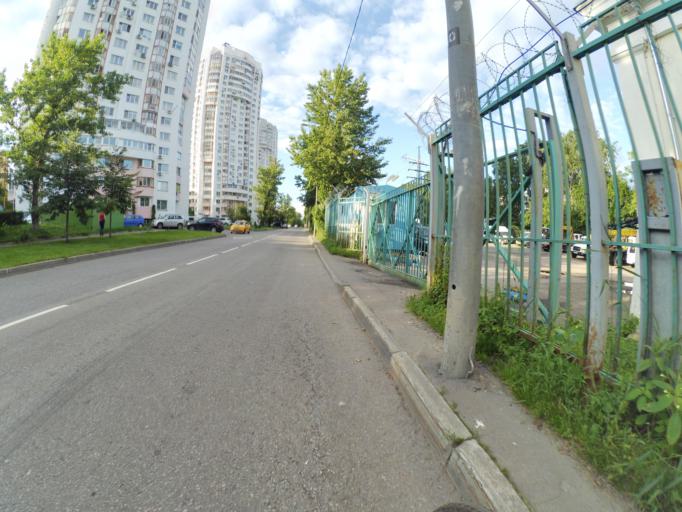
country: RU
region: Moscow
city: Pokrovskoye-Streshnevo
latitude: 55.8300
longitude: 37.4585
